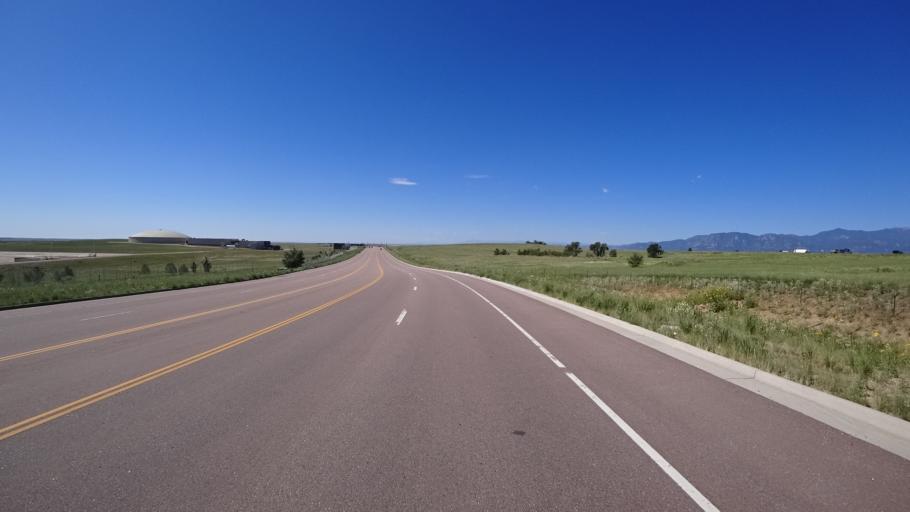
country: US
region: Colorado
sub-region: El Paso County
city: Cimarron Hills
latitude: 38.8483
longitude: -104.6827
